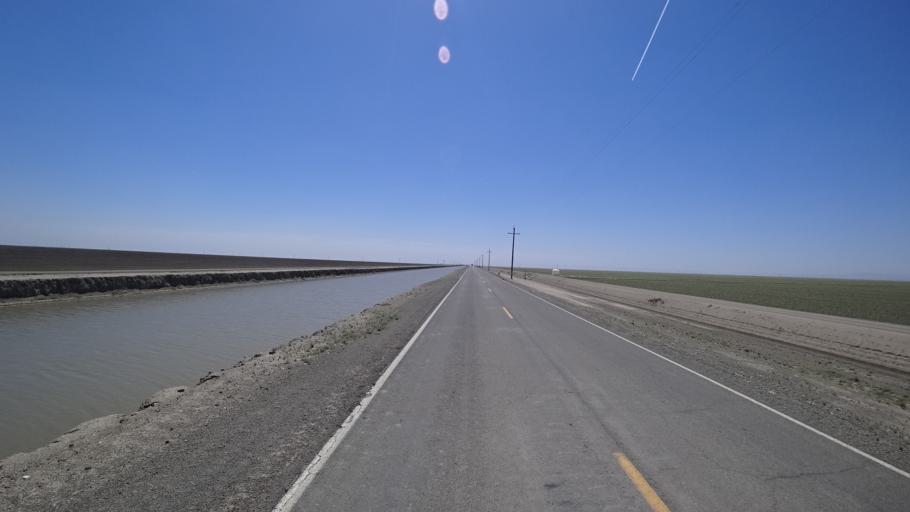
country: US
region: California
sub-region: Kings County
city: Corcoran
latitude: 36.0301
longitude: -119.6432
